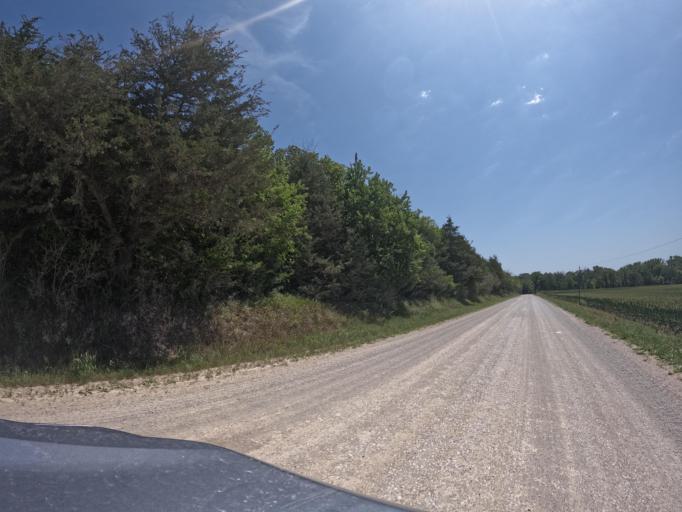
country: US
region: Iowa
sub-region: Henry County
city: Mount Pleasant
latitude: 40.8884
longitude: -91.5393
